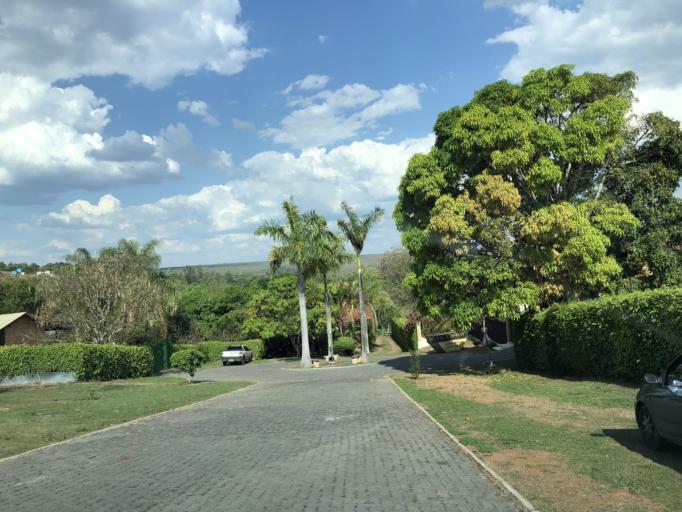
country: BR
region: Federal District
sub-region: Brasilia
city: Brasilia
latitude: -15.9086
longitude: -47.9272
